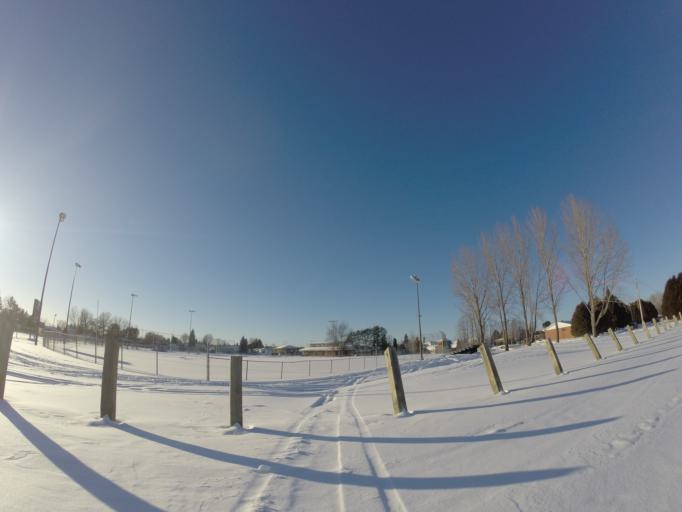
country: CA
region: Ontario
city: Rayside-Balfour
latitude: 46.5754
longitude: -81.1928
